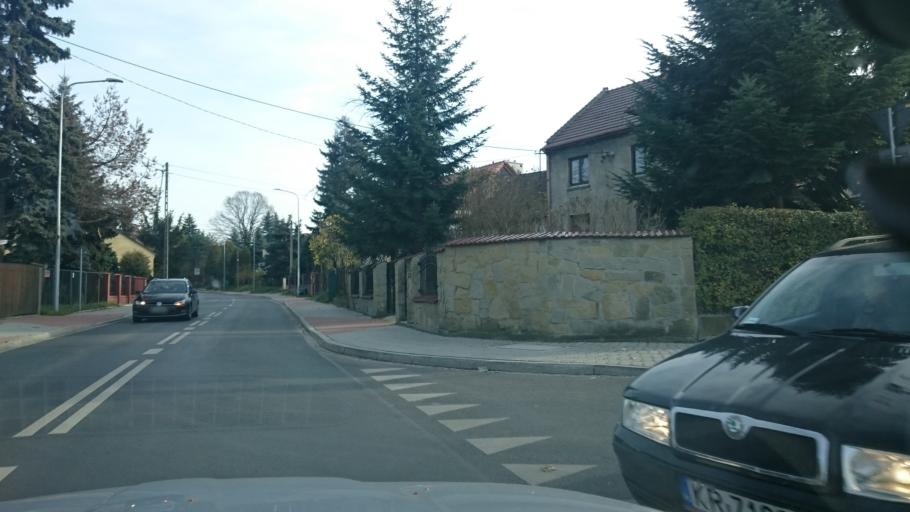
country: PL
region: Lesser Poland Voivodeship
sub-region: Powiat wielicki
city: Czarnochowice
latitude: 50.0190
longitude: 20.0248
